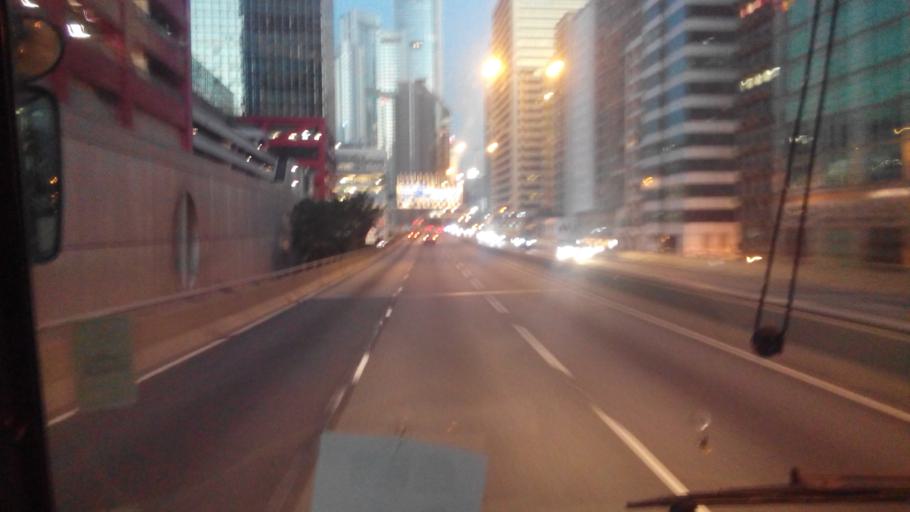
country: HK
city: Hong Kong
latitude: 22.2879
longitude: 114.1506
